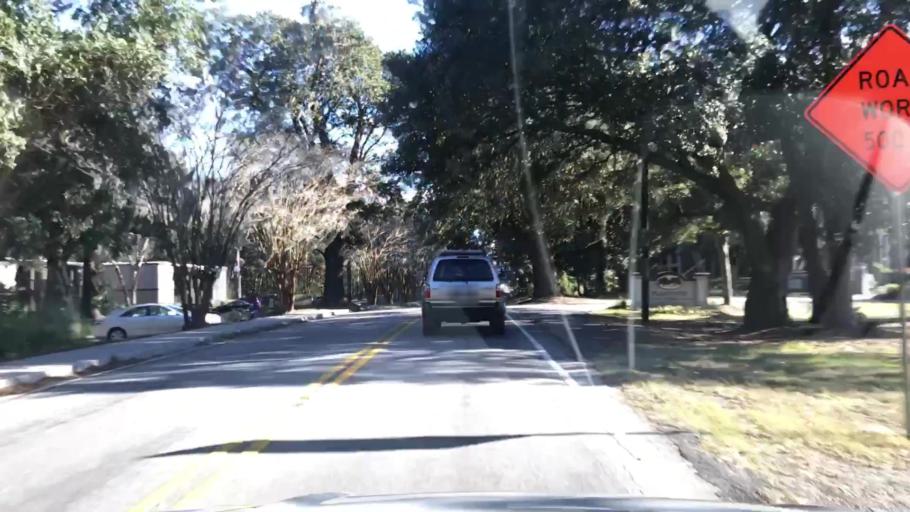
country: US
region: South Carolina
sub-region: Charleston County
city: North Charleston
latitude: 32.8181
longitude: -80.0337
